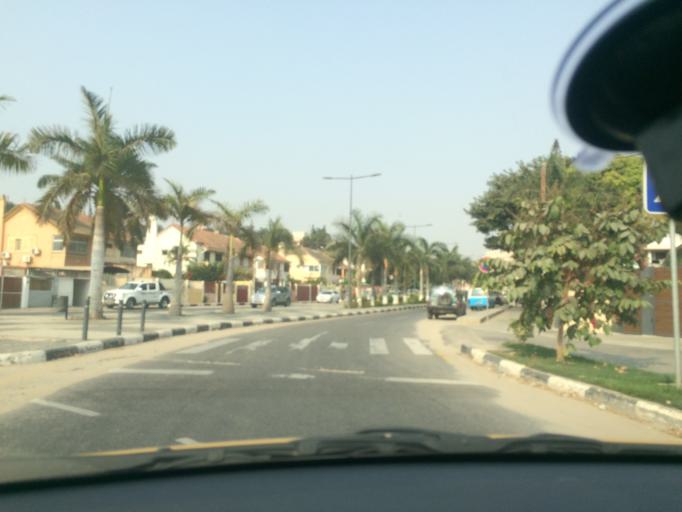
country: AO
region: Luanda
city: Luanda
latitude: -8.8204
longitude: 13.2193
